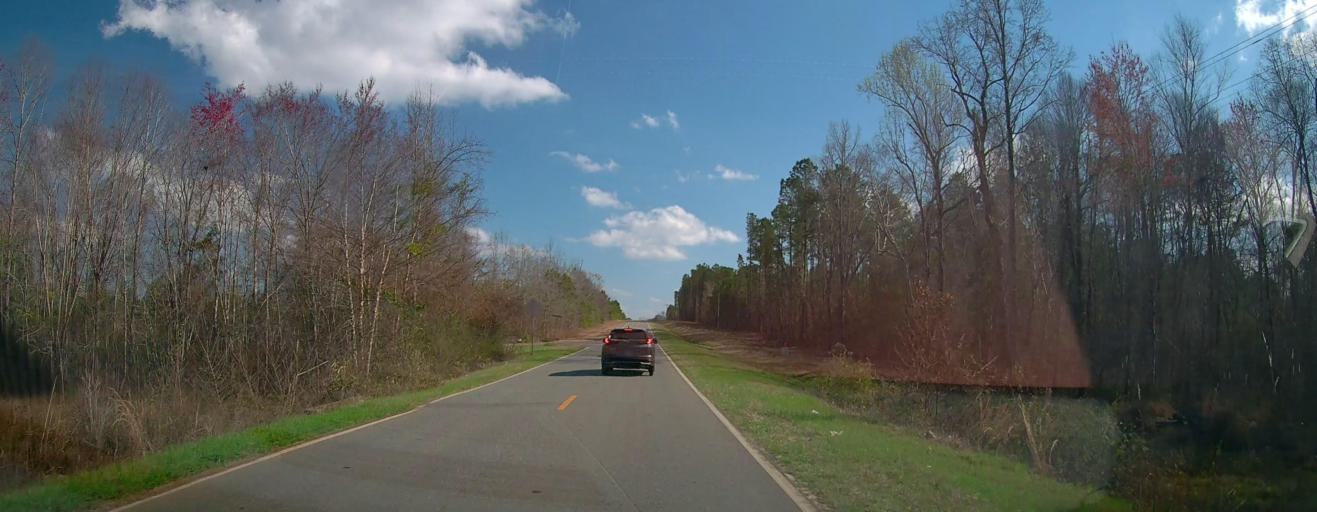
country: US
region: Georgia
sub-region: Laurens County
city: Dublin
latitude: 32.6046
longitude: -83.0759
